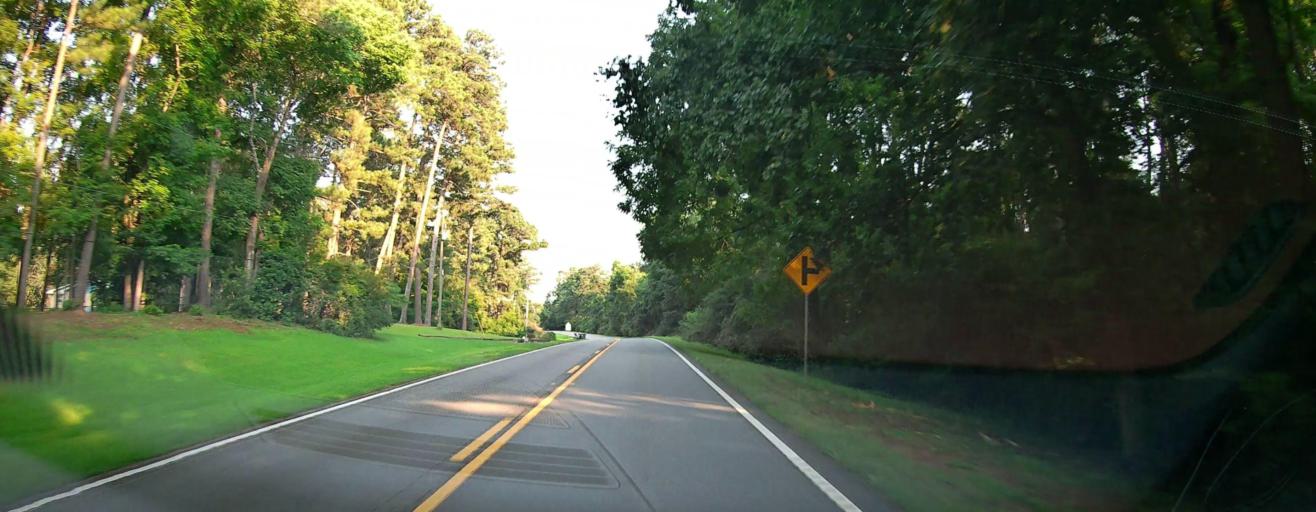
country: US
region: Georgia
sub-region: Bibb County
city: West Point
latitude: 32.8983
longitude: -83.7657
